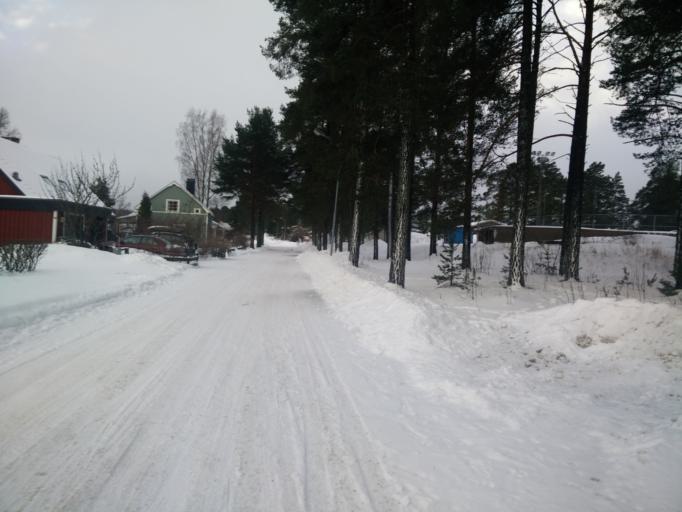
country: SE
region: Vaesternorrland
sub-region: Sundsvalls Kommun
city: Nolby
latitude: 62.2913
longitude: 17.3648
